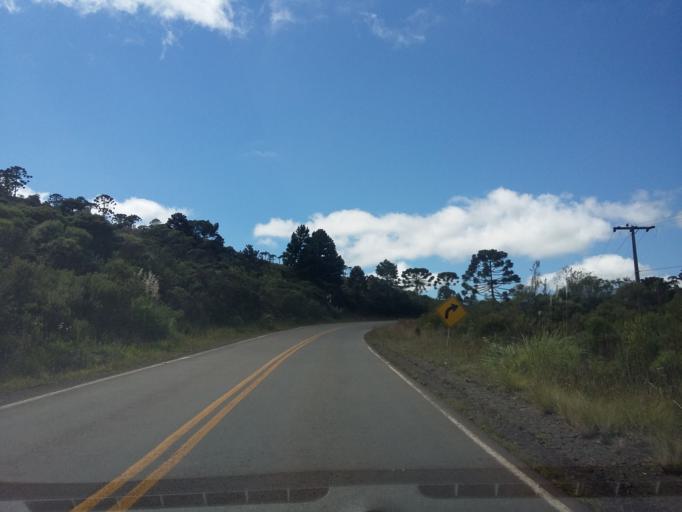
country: BR
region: Santa Catarina
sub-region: Sao Joaquim
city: Sao Joaquim
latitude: -28.2381
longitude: -49.8173
